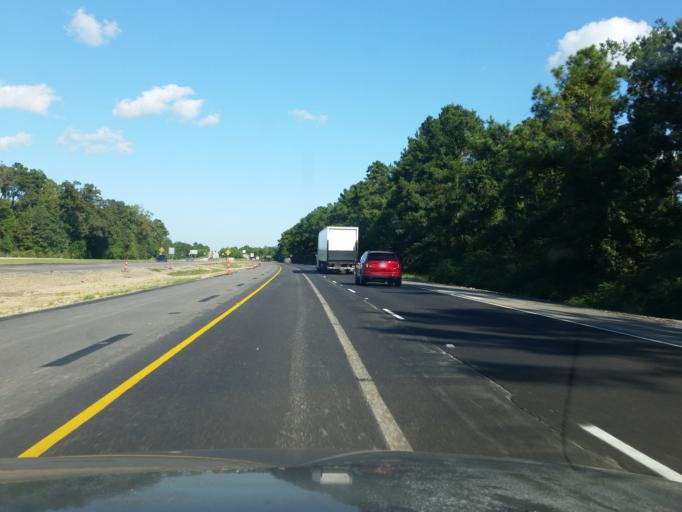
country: US
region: Louisiana
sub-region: Saint Tammany Parish
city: Slidell
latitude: 30.2982
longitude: -89.7117
